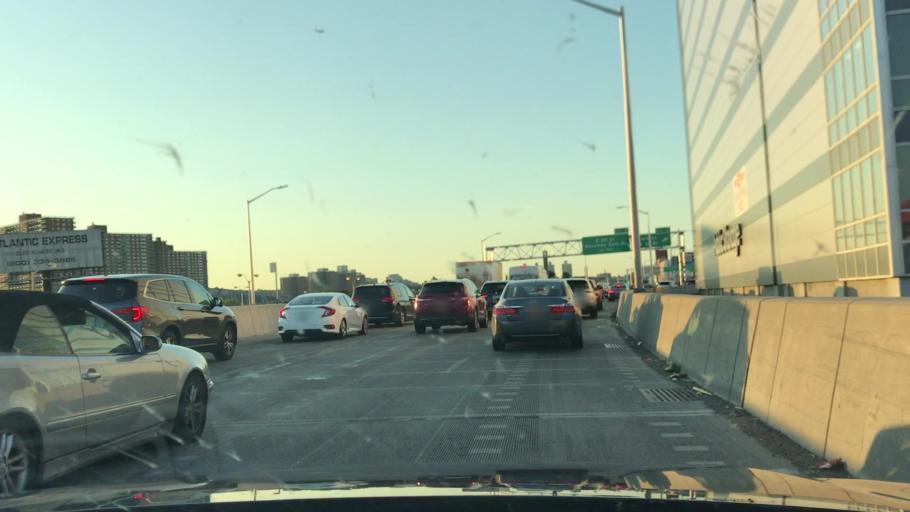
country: US
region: New Jersey
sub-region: Bergen County
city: Edgewater
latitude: 40.8162
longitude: -73.9308
